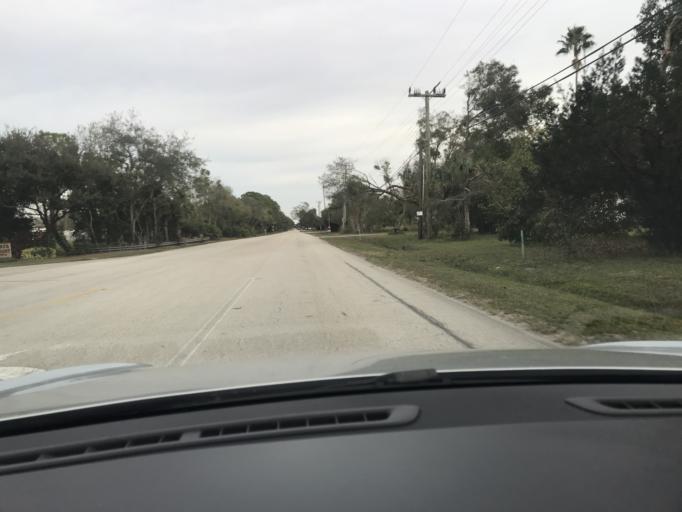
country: US
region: Florida
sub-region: Saint Lucie County
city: Lakewood Park
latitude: 27.4840
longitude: -80.3801
